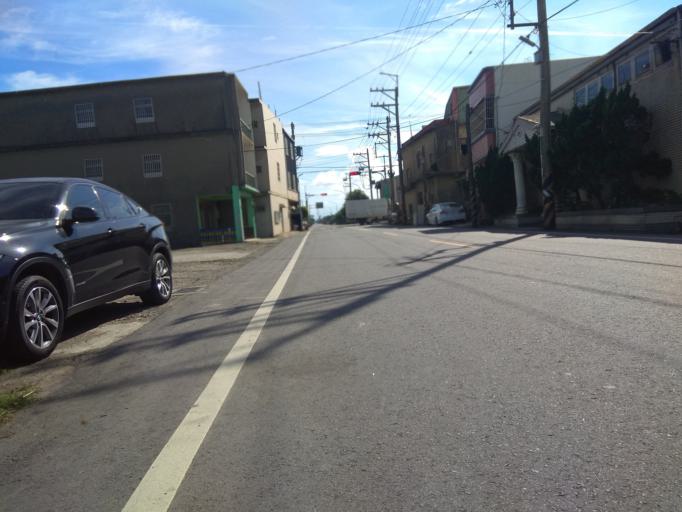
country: TW
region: Taiwan
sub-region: Hsinchu
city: Zhubei
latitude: 25.0081
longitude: 121.0436
